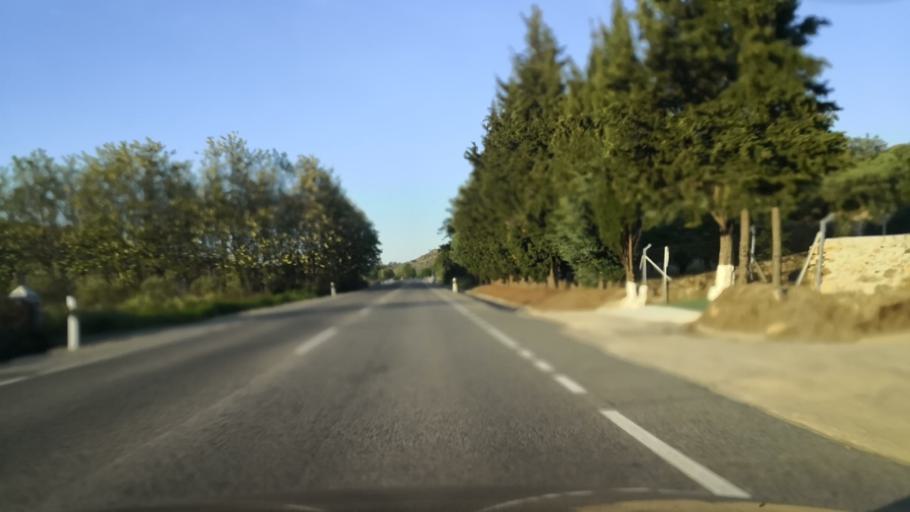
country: ES
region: Extremadura
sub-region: Provincia de Caceres
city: Valencia de Alcantara
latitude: 39.3709
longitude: -7.2635
